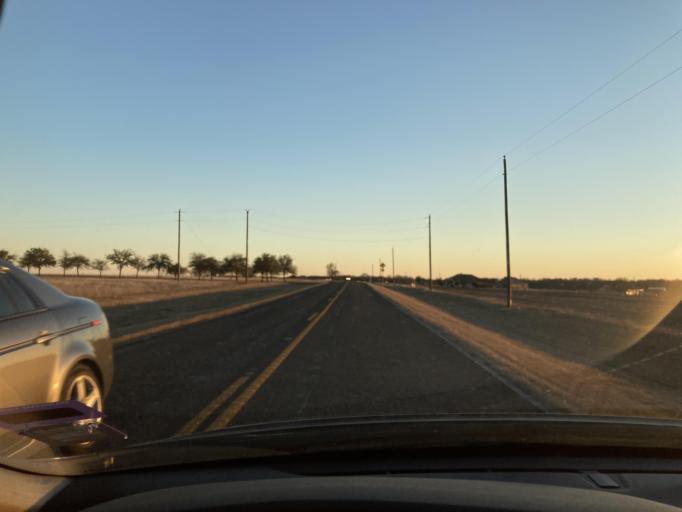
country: US
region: Texas
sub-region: Ellis County
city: Waxahachie
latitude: 32.3199
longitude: -96.8783
